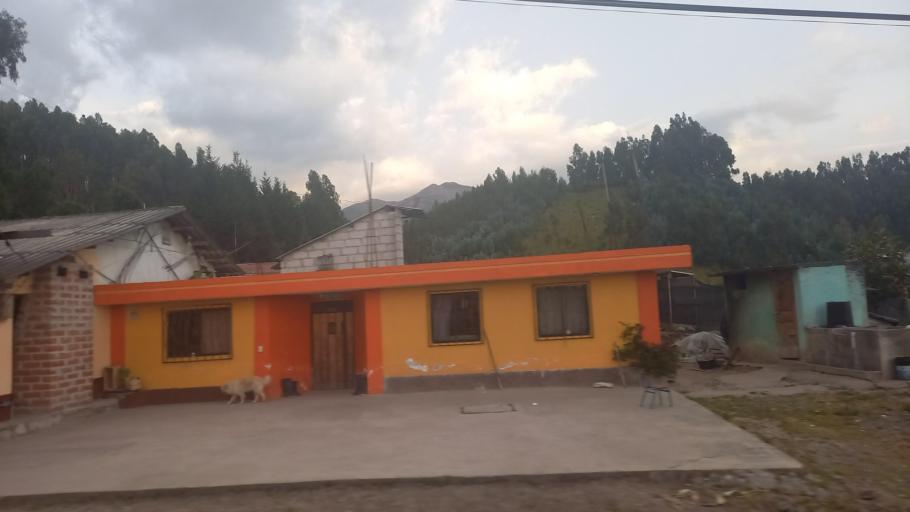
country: EC
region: Pichincha
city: Cayambe
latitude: 0.0831
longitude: -78.1055
